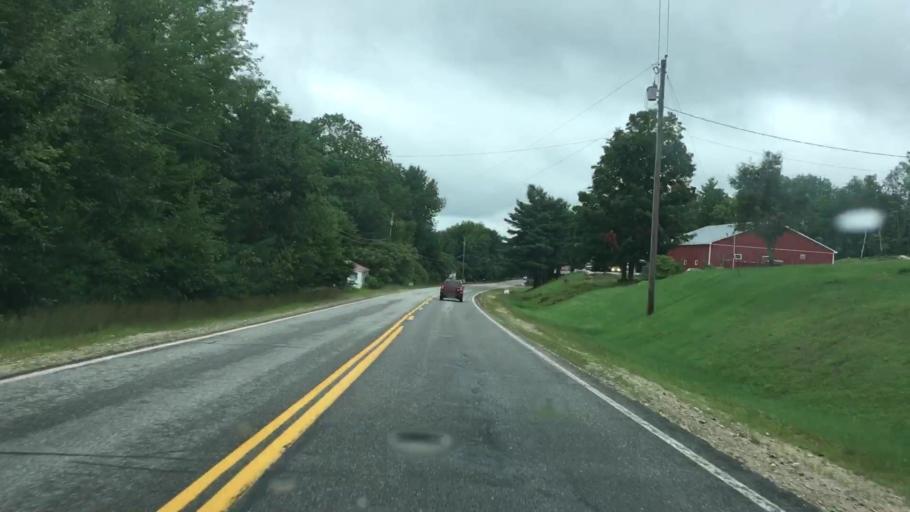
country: US
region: Maine
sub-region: Oxford County
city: Brownfield
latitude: 43.9633
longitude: -70.9063
